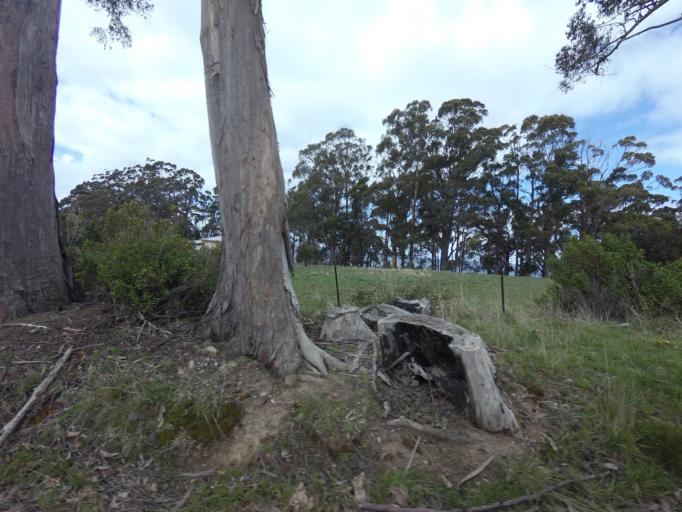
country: AU
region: Tasmania
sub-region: Huon Valley
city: Cygnet
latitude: -43.4136
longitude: 147.0177
